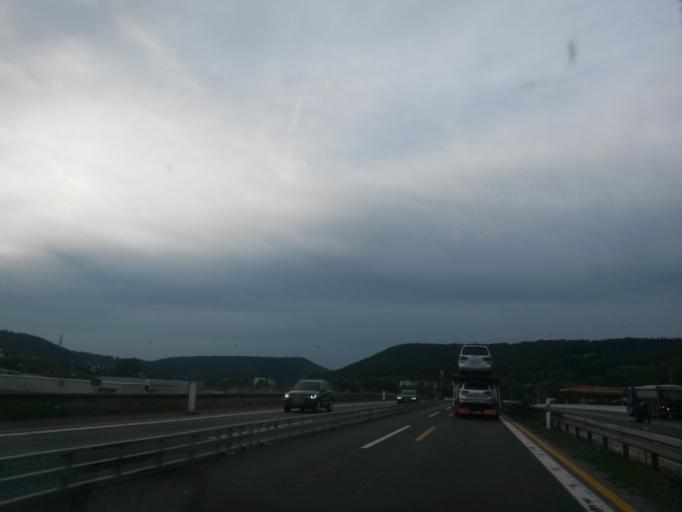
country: DE
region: Bavaria
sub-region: Regierungsbezirk Mittelfranken
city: Greding
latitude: 49.0481
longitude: 11.3353
